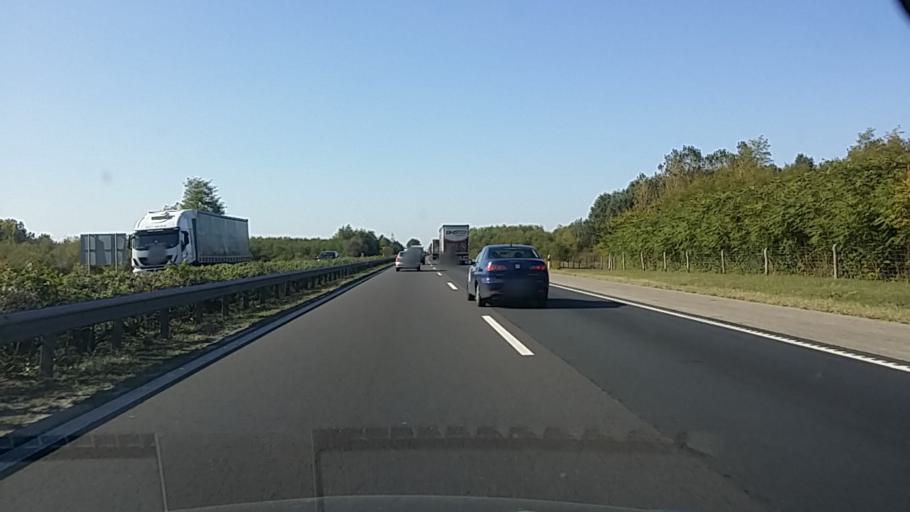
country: HU
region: Pest
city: Felsopakony
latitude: 47.3265
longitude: 19.2395
